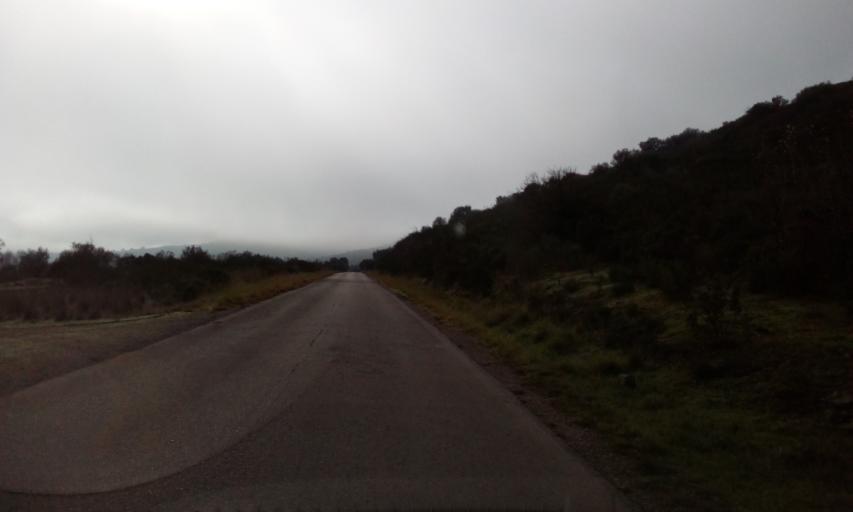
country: ES
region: Andalusia
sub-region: Provincia de Huelva
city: Sanlucar de Guadiana
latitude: 37.4394
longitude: -7.4622
